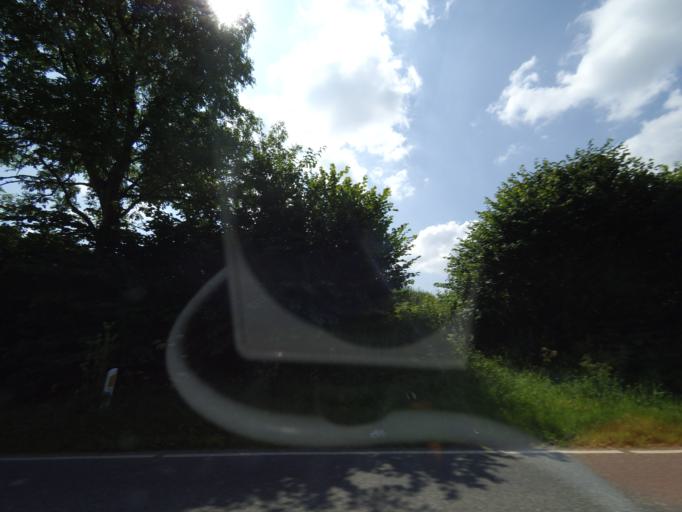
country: DK
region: South Denmark
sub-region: Assens Kommune
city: Arup
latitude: 55.3941
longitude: 10.0501
